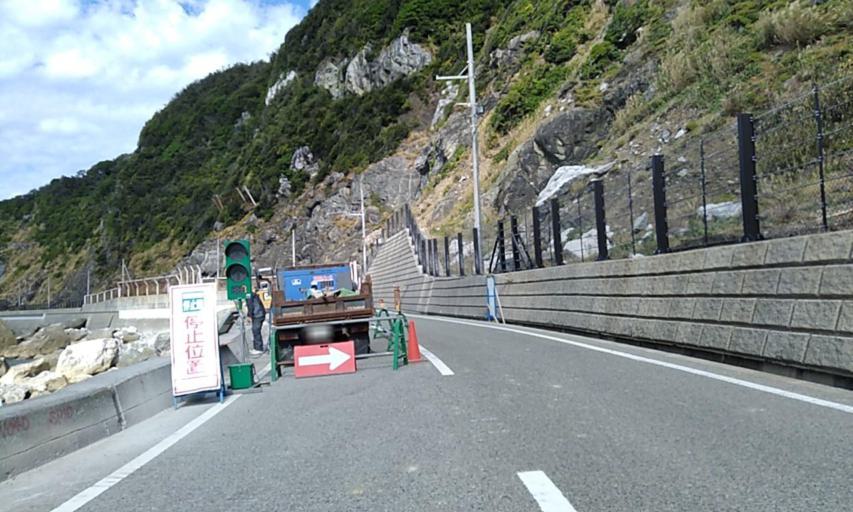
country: JP
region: Wakayama
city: Gobo
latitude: 33.9747
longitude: 135.0764
